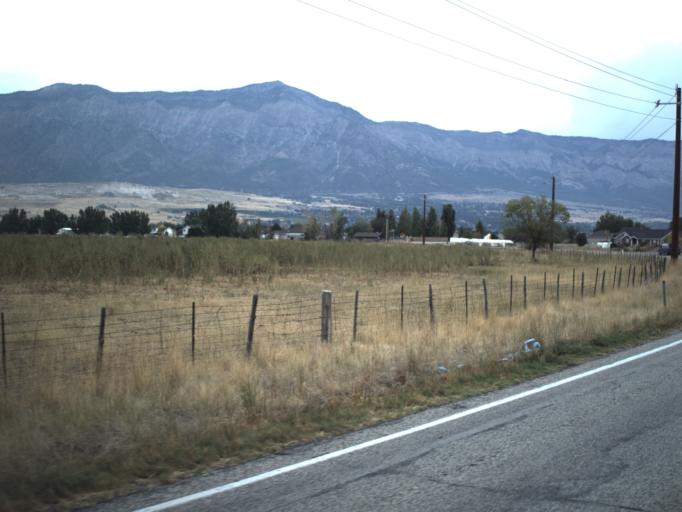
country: US
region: Utah
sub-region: Weber County
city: Farr West
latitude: 41.3050
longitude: -112.0483
